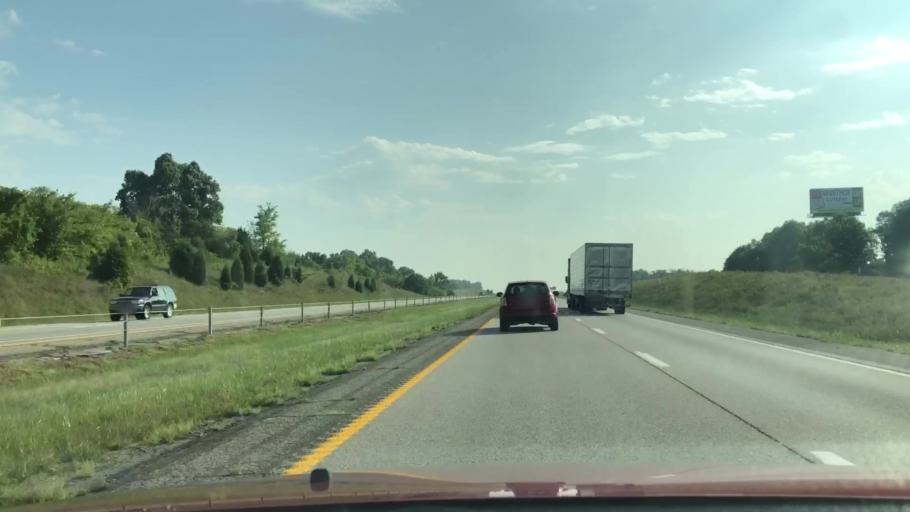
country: US
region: Missouri
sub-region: Laclede County
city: Lebanon
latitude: 37.5858
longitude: -92.7374
